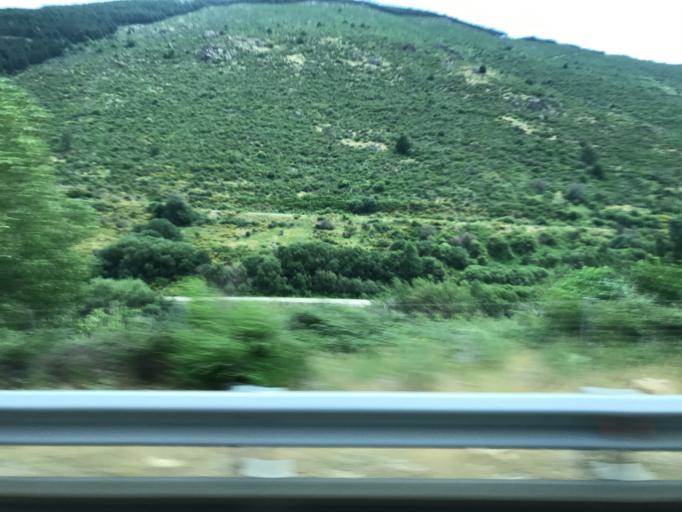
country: ES
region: Madrid
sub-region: Provincia de Madrid
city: Somosierra
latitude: 41.1567
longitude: -3.5844
